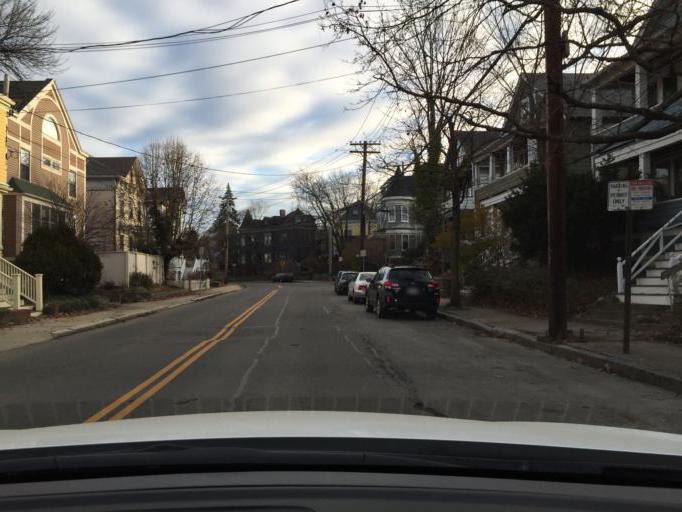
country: US
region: Massachusetts
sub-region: Middlesex County
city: Cambridge
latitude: 42.3876
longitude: -71.1267
